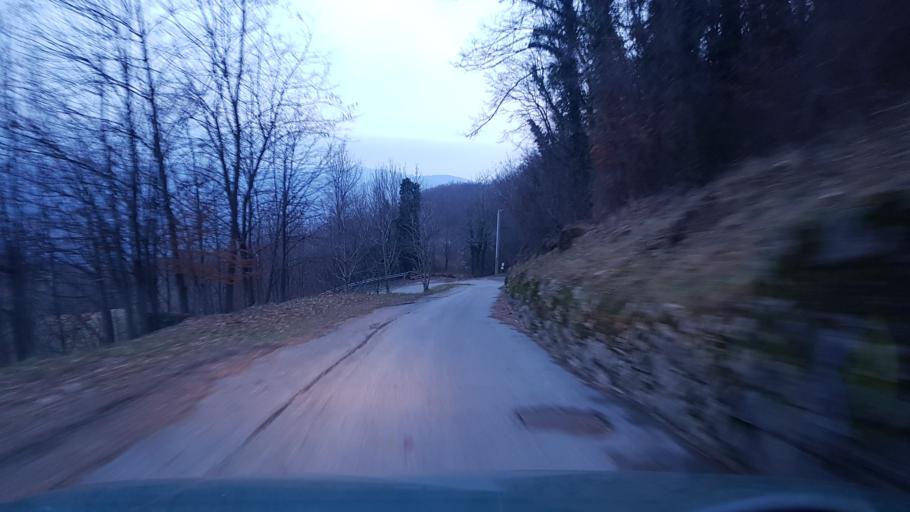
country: IT
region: Friuli Venezia Giulia
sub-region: Provincia di Udine
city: Pulfero
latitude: 46.1472
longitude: 13.4640
